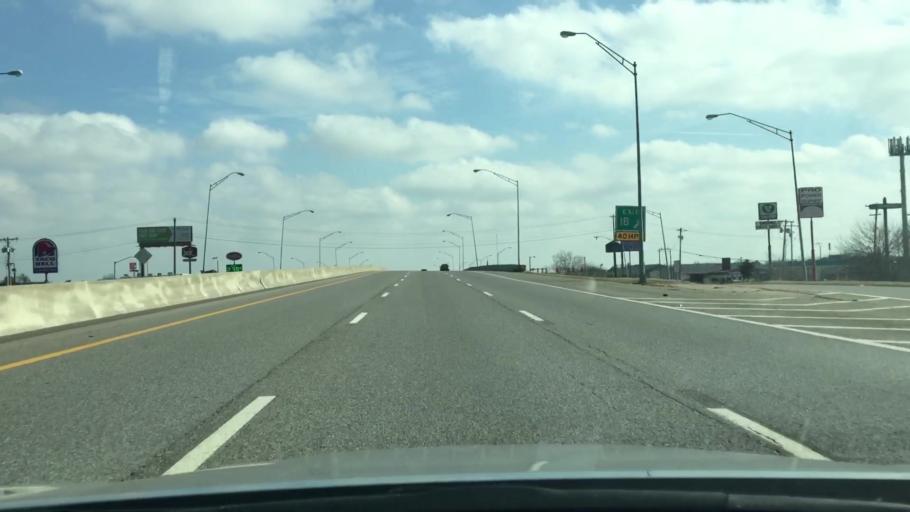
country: US
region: Oklahoma
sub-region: Oklahoma County
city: Oklahoma City
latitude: 35.3943
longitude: -97.5676
